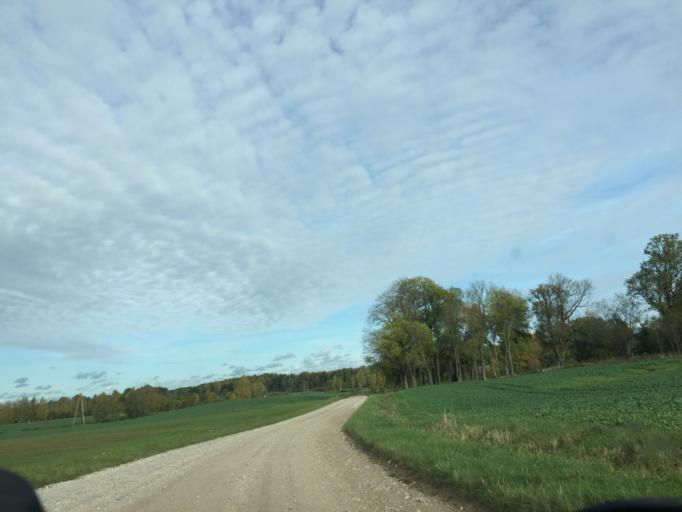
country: LV
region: Jaunpils
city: Jaunpils
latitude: 56.6156
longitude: 23.0658
